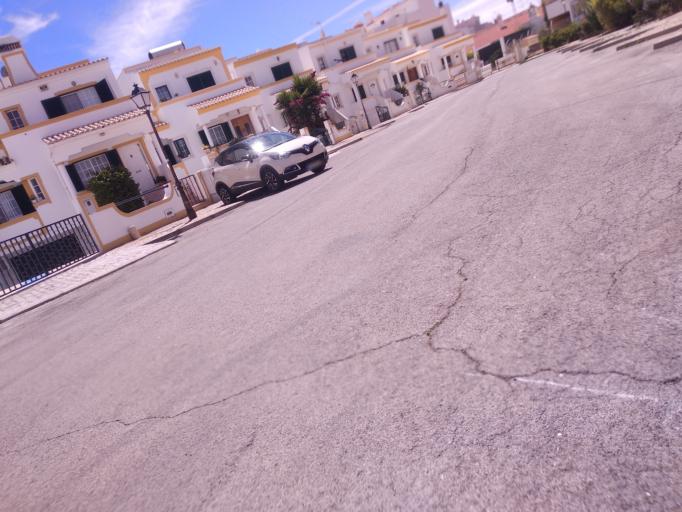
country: PT
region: Faro
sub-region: Sao Bras de Alportel
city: Sao Bras de Alportel
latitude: 37.1561
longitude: -7.8844
